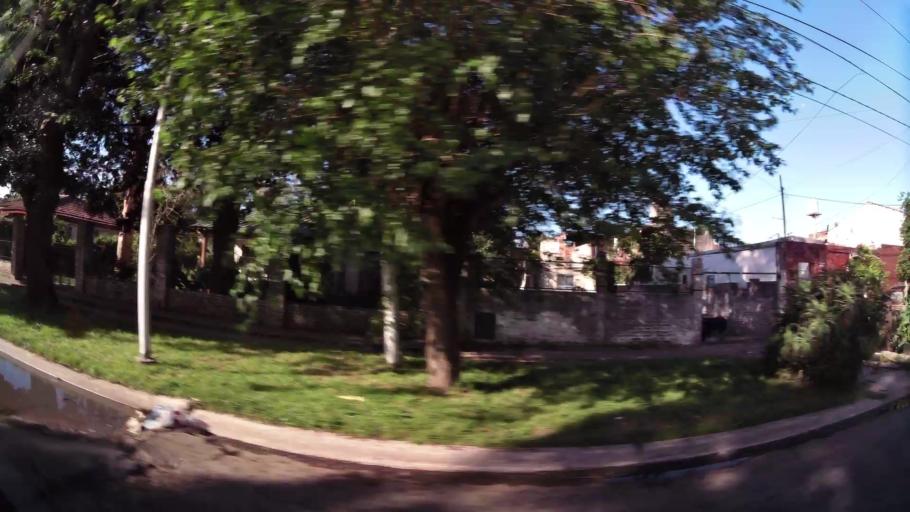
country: AR
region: Buenos Aires
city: Santa Catalina - Dique Lujan
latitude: -34.4878
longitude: -58.7192
